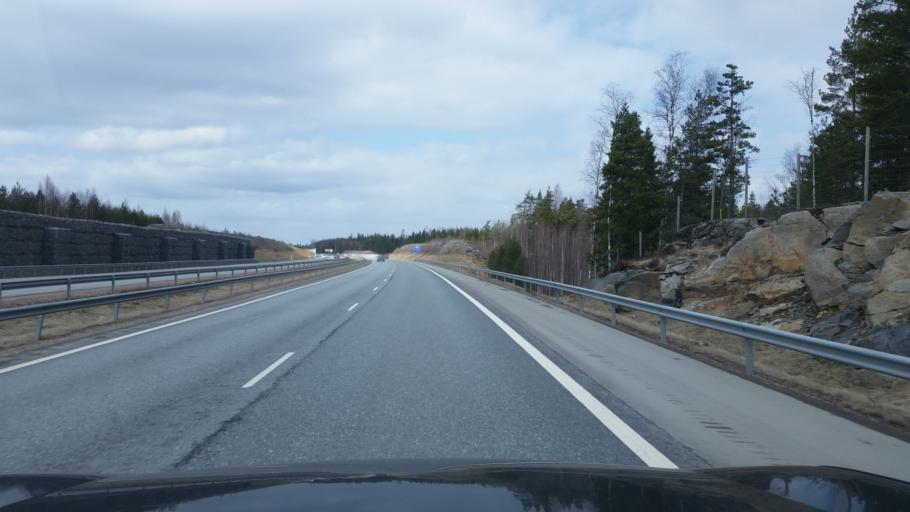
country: FI
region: Uusimaa
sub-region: Helsinki
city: Sammatti
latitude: 60.3630
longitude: 23.8822
